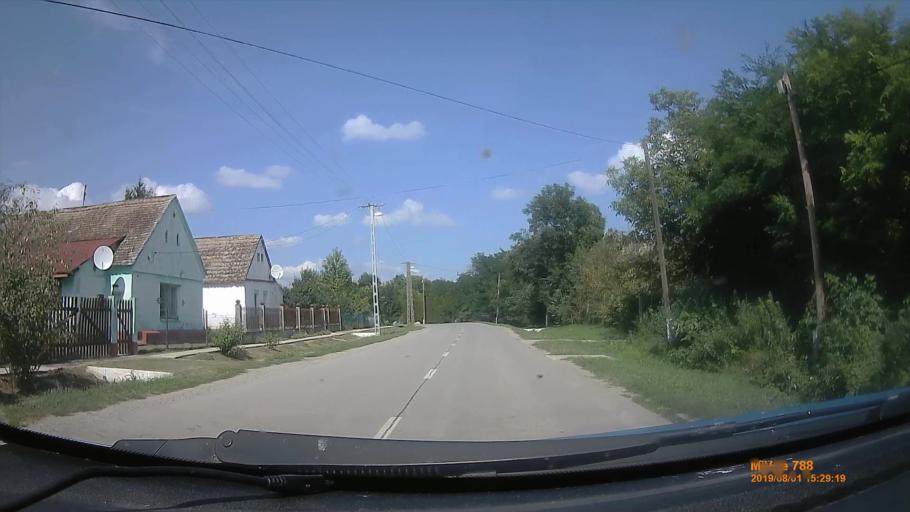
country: HU
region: Baranya
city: Sellye
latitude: 45.9227
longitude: 17.8712
